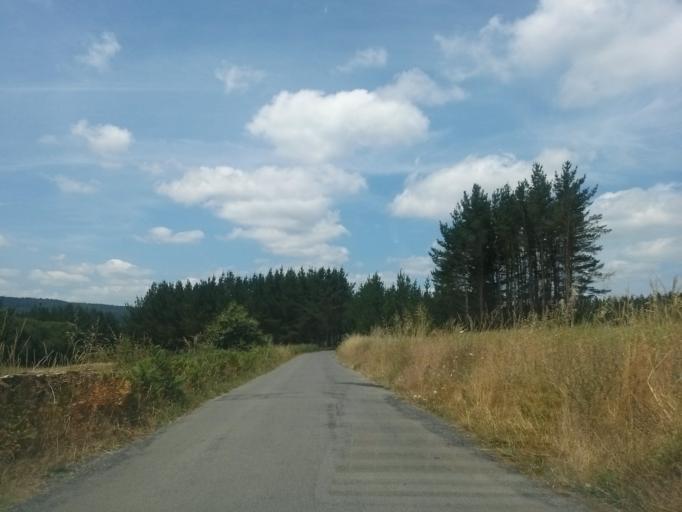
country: ES
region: Galicia
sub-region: Provincia de Lugo
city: Lugo
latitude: 43.0376
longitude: -7.6044
